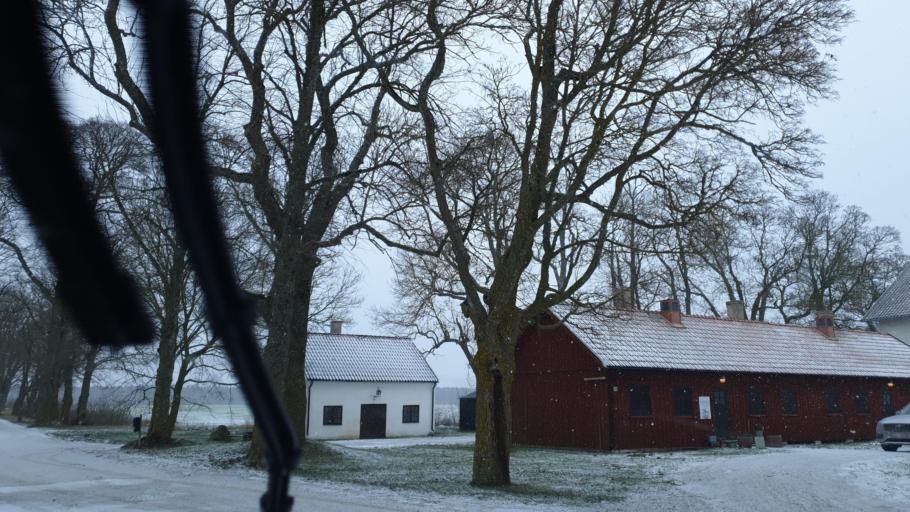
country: SE
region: Gotland
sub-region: Gotland
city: Visby
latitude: 57.5163
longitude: 18.4586
